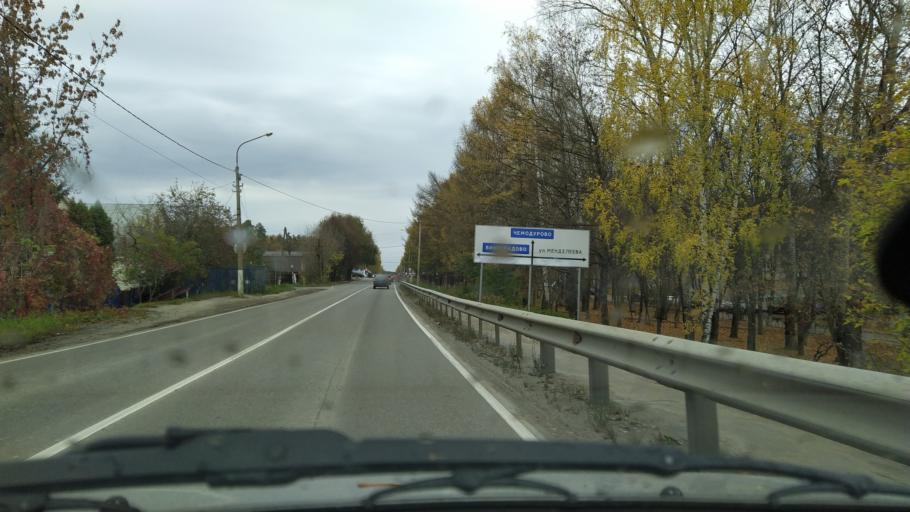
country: RU
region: Moskovskaya
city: Voskresensk
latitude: 55.3241
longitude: 38.6542
